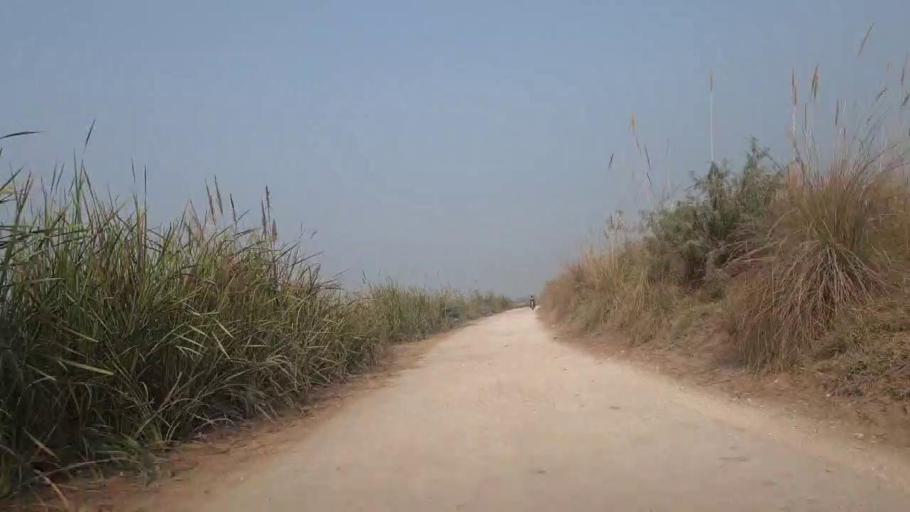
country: PK
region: Sindh
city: Shahdadpur
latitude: 25.8939
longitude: 68.5904
